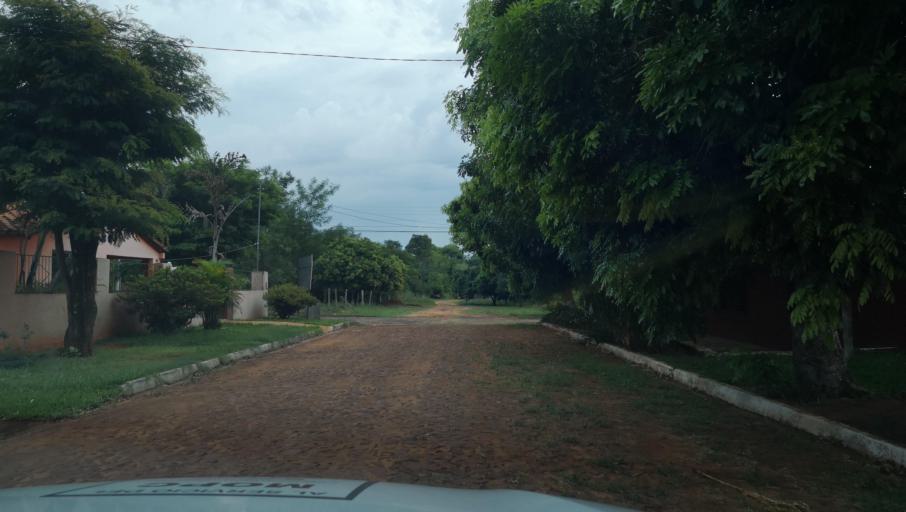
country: PY
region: Misiones
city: Santa Maria
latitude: -26.8829
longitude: -57.0375
